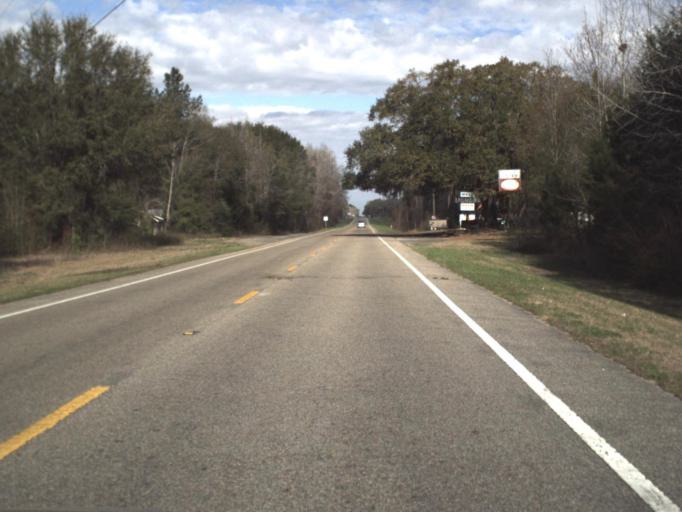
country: US
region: Florida
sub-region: Jackson County
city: Malone
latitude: 30.9952
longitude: -85.1971
